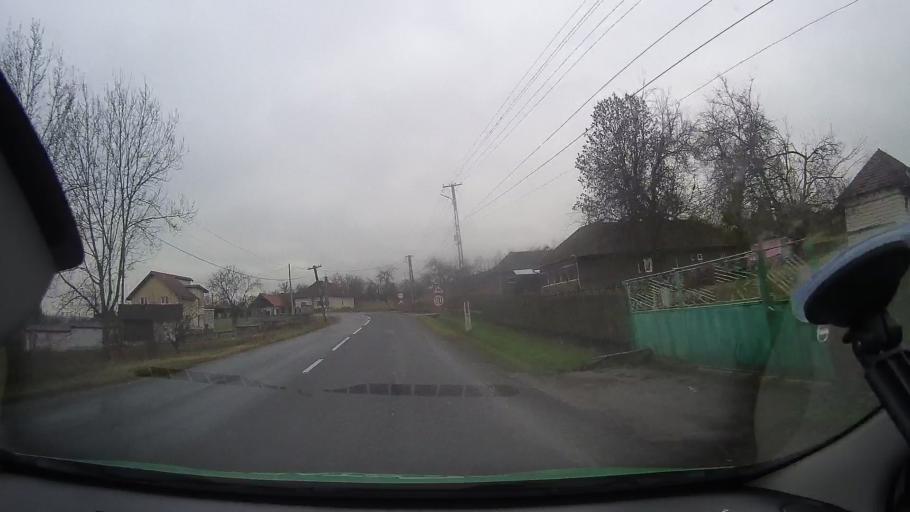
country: RO
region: Arad
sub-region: Comuna Varfurile
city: Varfurile
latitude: 46.3176
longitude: 22.5088
